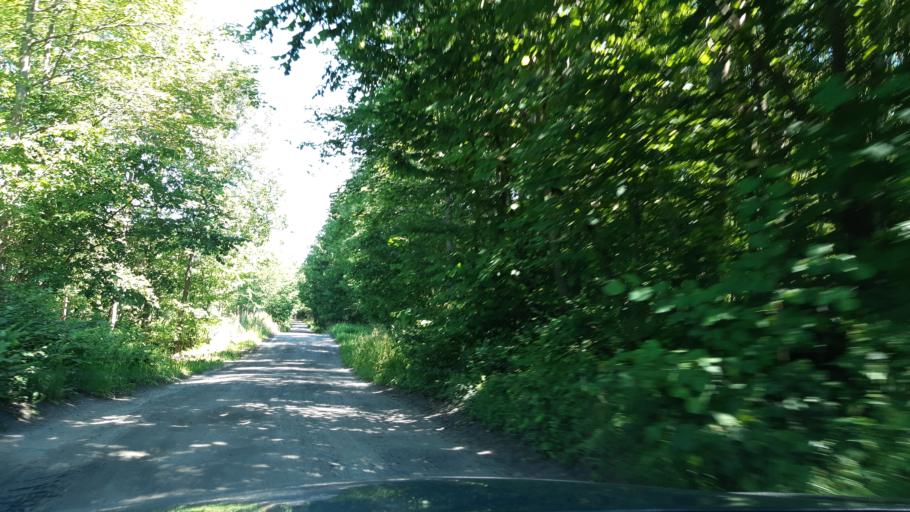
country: PL
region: Warmian-Masurian Voivodeship
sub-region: Powiat piski
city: Ruciane-Nida
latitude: 53.7024
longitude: 21.4734
